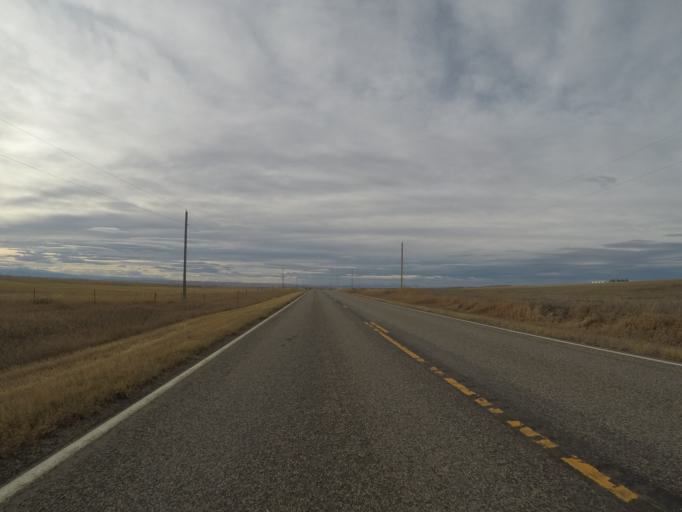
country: US
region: Montana
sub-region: Yellowstone County
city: Laurel
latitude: 45.8563
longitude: -108.8013
